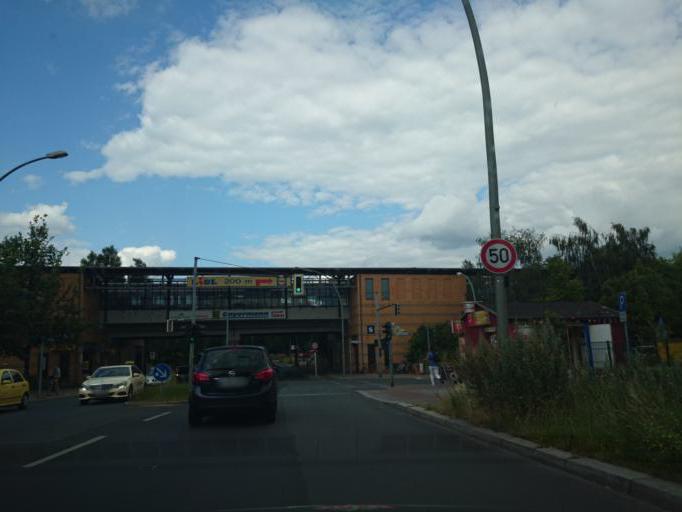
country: DE
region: Berlin
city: Lichtenrade
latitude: 52.3983
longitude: 13.3885
